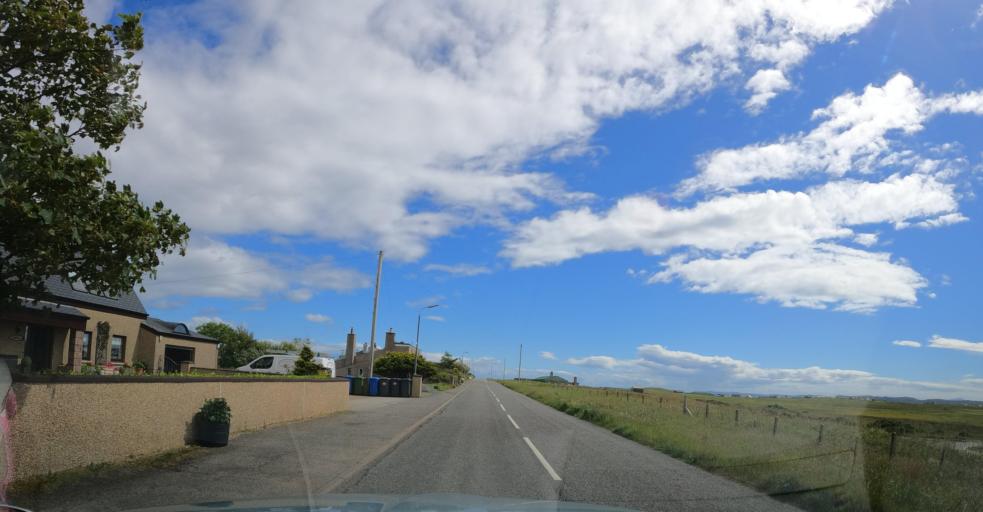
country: GB
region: Scotland
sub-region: Eilean Siar
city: Stornoway
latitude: 58.2077
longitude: -6.3221
